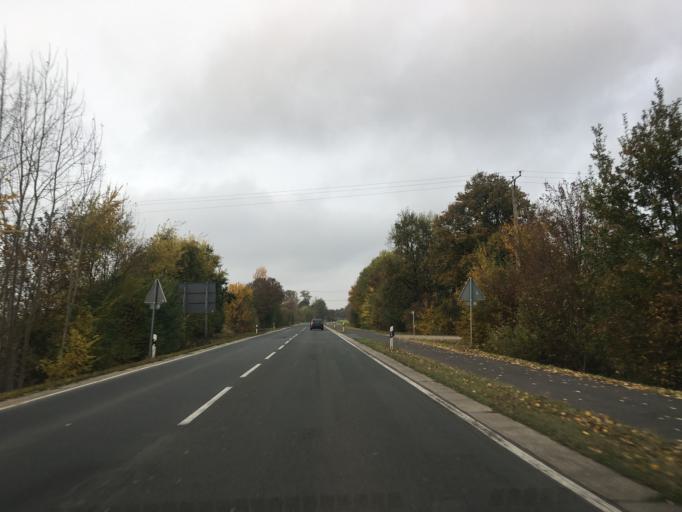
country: DE
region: North Rhine-Westphalia
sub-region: Regierungsbezirk Munster
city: Altenberge
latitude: 52.0742
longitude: 7.4354
